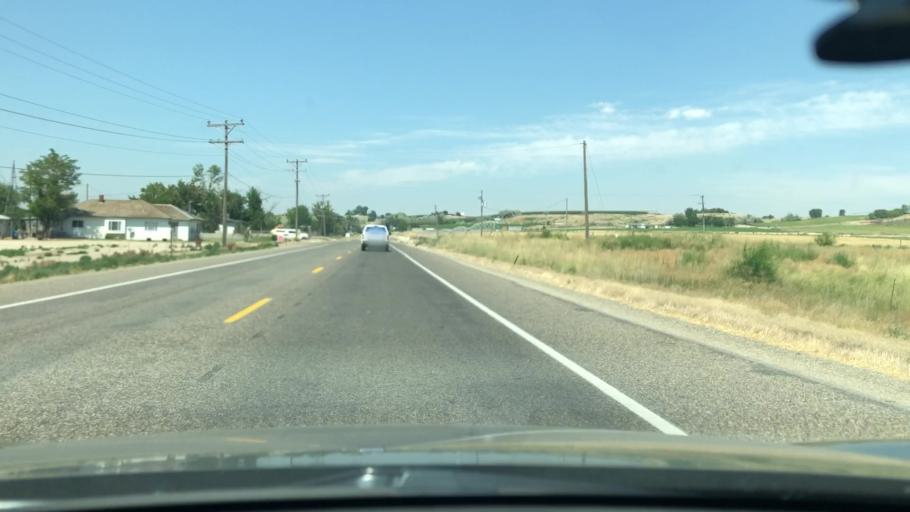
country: US
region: Idaho
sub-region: Canyon County
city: Wilder
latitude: 43.6455
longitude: -116.9117
